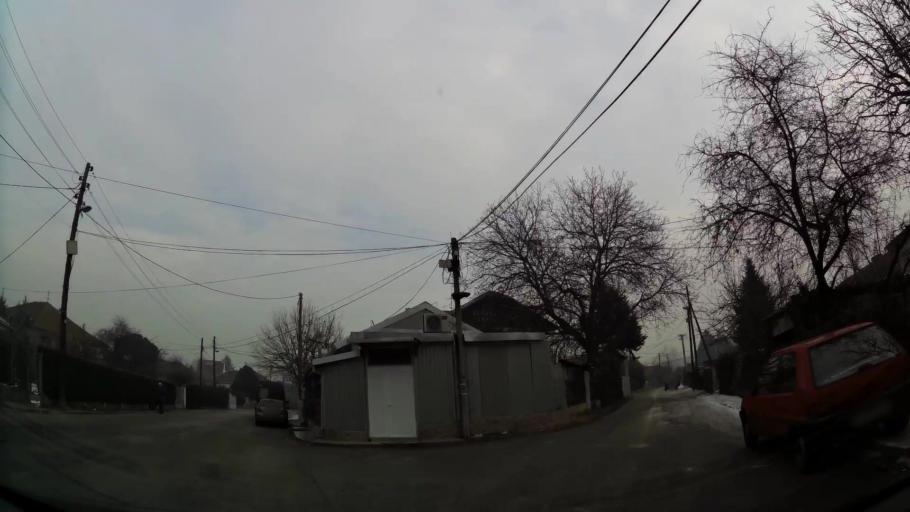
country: MK
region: Kisela Voda
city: Kisela Voda
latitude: 41.9986
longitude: 21.4956
